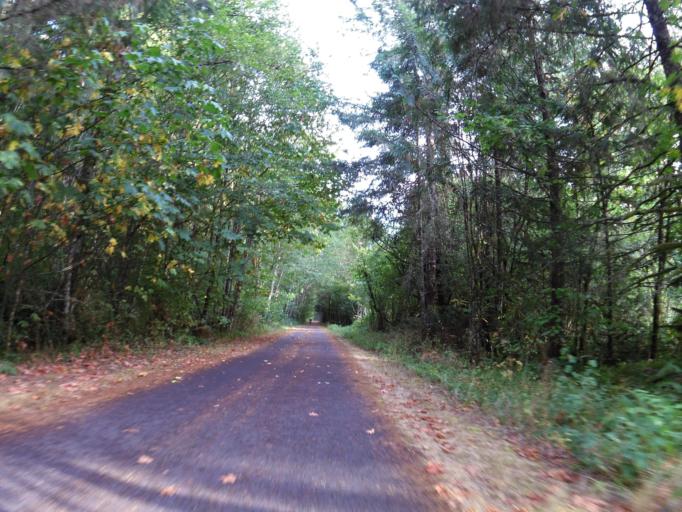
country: US
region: Washington
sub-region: Thurston County
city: Tenino
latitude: 46.9263
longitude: -122.8109
